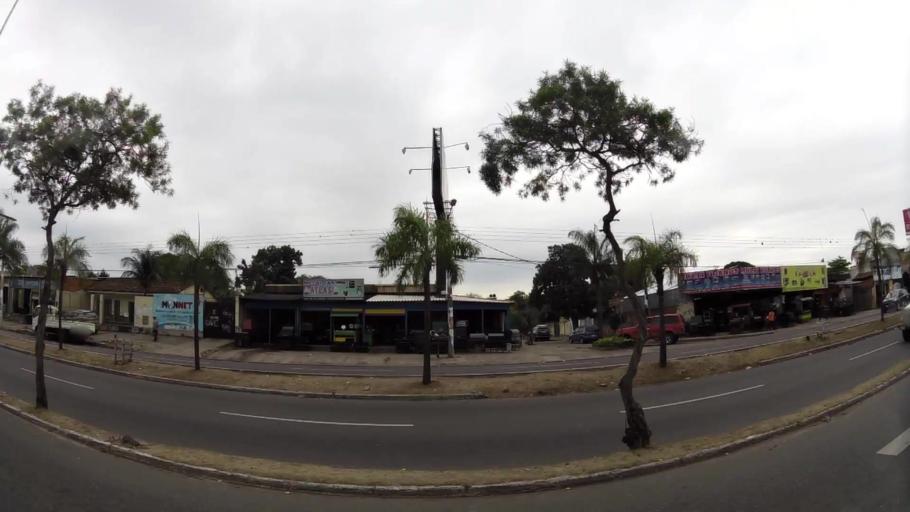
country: BO
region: Santa Cruz
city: Santa Cruz de la Sierra
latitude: -17.8012
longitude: -63.1869
